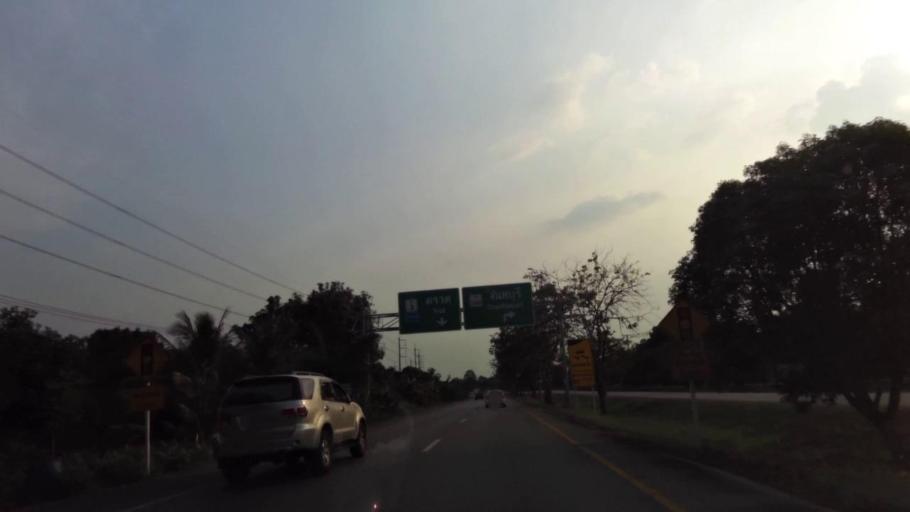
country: TH
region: Chanthaburi
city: Chanthaburi
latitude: 12.5325
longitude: 102.1574
